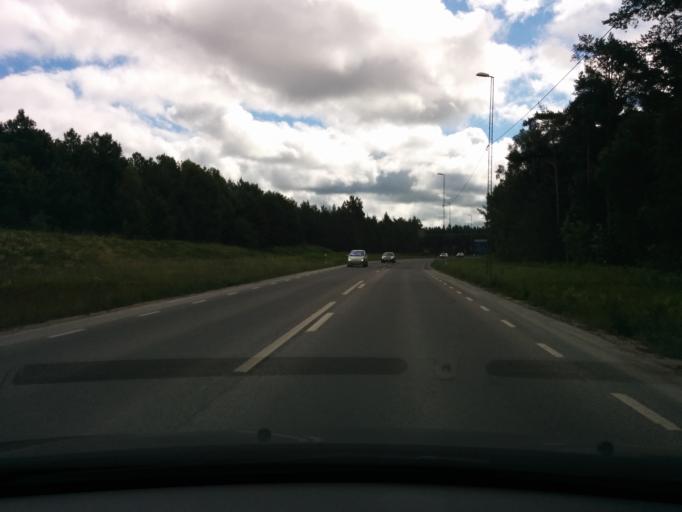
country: SE
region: Gotland
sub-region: Gotland
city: Visby
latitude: 57.6100
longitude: 18.2959
